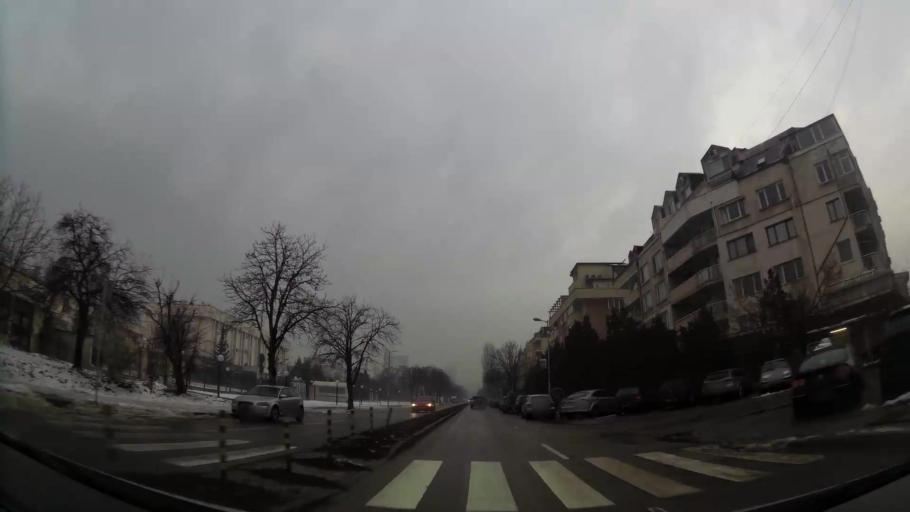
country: BG
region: Sofia-Capital
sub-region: Stolichna Obshtina
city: Sofia
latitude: 42.6748
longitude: 23.2618
